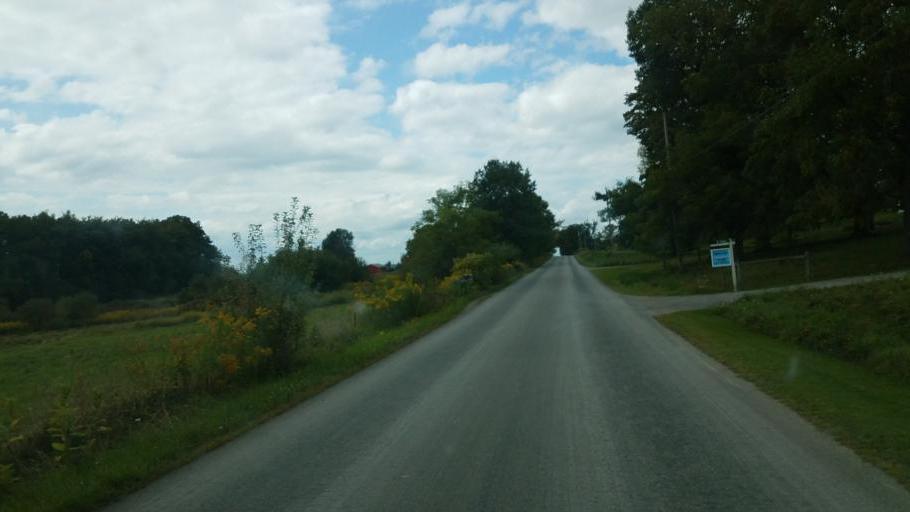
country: US
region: Pennsylvania
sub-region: Crawford County
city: Conneaut Lakeshore
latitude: 41.5039
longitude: -80.3040
